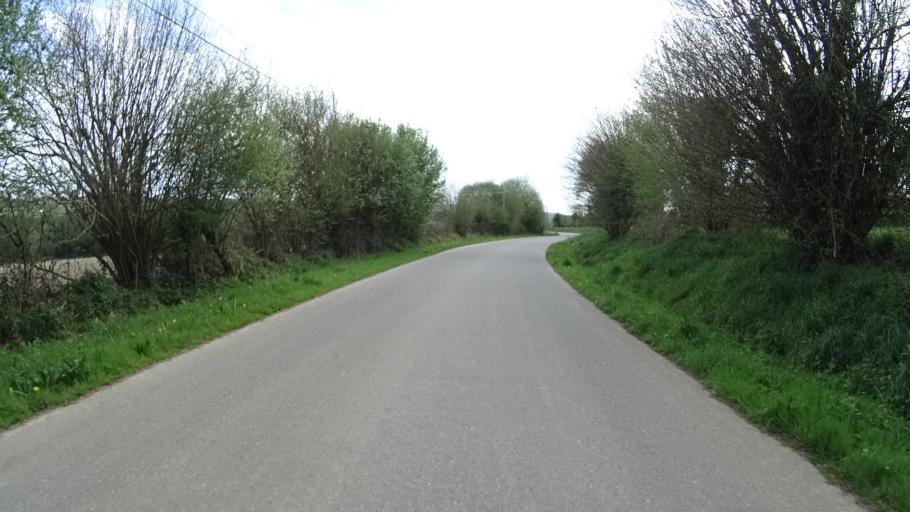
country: FR
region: Brittany
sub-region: Departement du Finistere
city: Sizun
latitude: 48.4151
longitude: -4.0589
